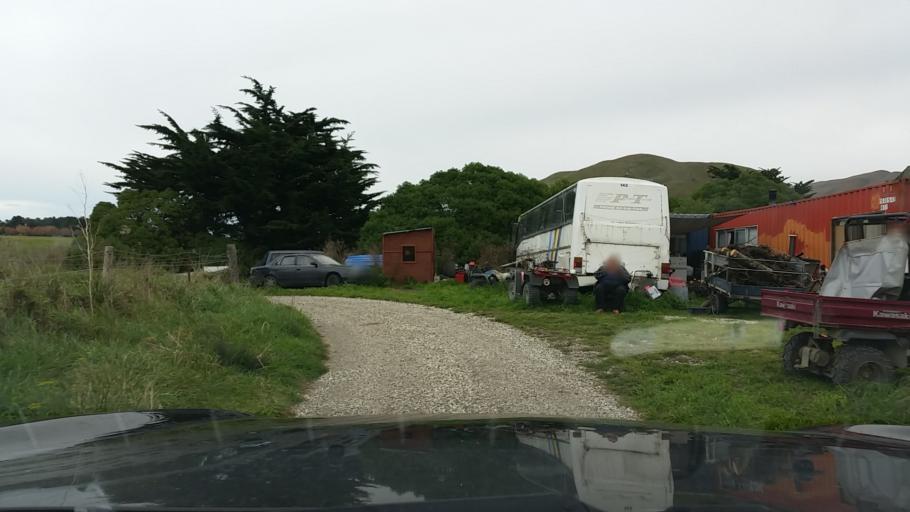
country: NZ
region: Marlborough
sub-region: Marlborough District
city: Blenheim
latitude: -41.9250
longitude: 174.0933
